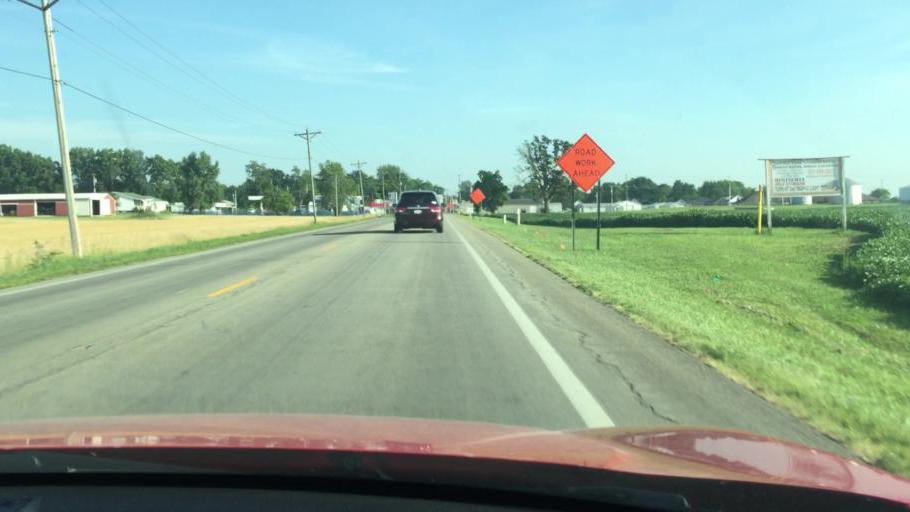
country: US
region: Ohio
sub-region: Logan County
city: Northwood
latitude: 40.4505
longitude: -83.8073
